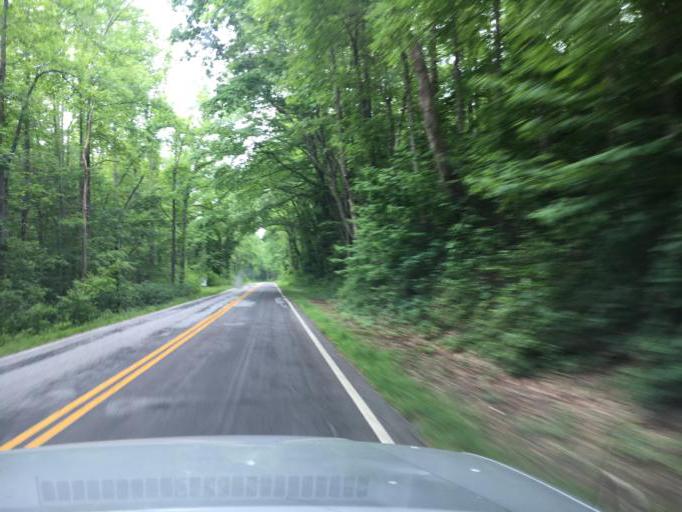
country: US
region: North Carolina
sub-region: Henderson County
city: Flat Rock
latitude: 35.1832
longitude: -82.4123
